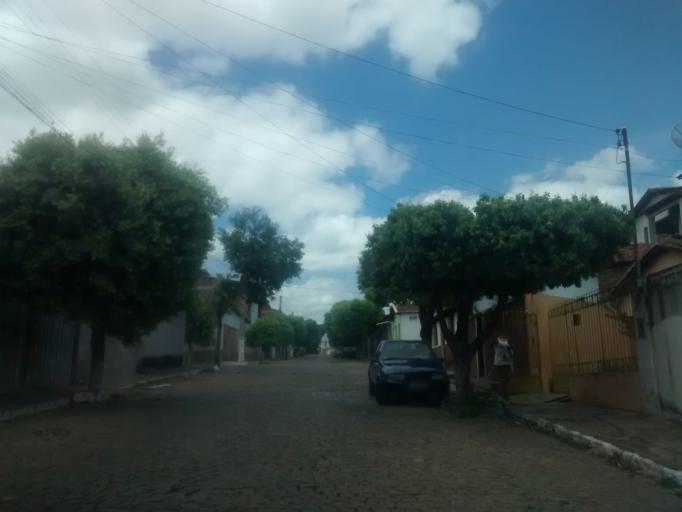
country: BR
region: Bahia
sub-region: Brumado
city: Brumado
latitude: -14.2007
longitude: -41.6714
